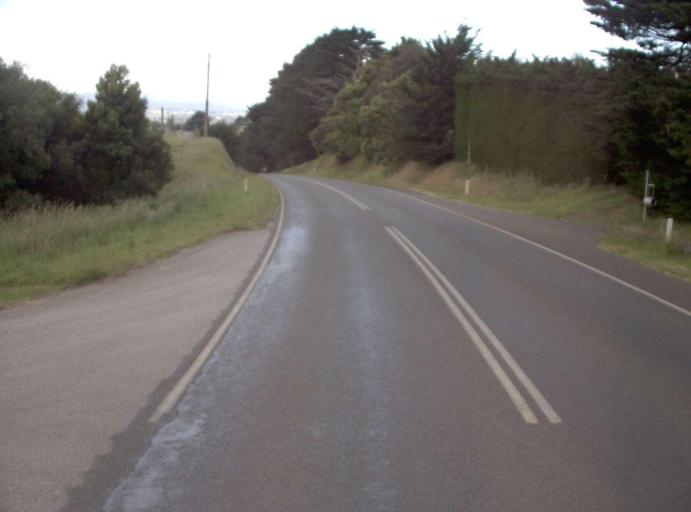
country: AU
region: Victoria
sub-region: Baw Baw
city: Warragul
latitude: -38.1116
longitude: 145.9256
